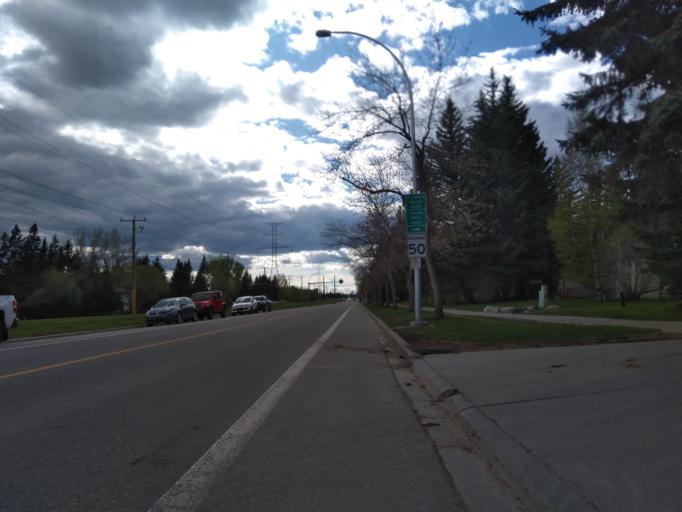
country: CA
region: Alberta
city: Calgary
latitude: 50.9946
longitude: -114.1294
